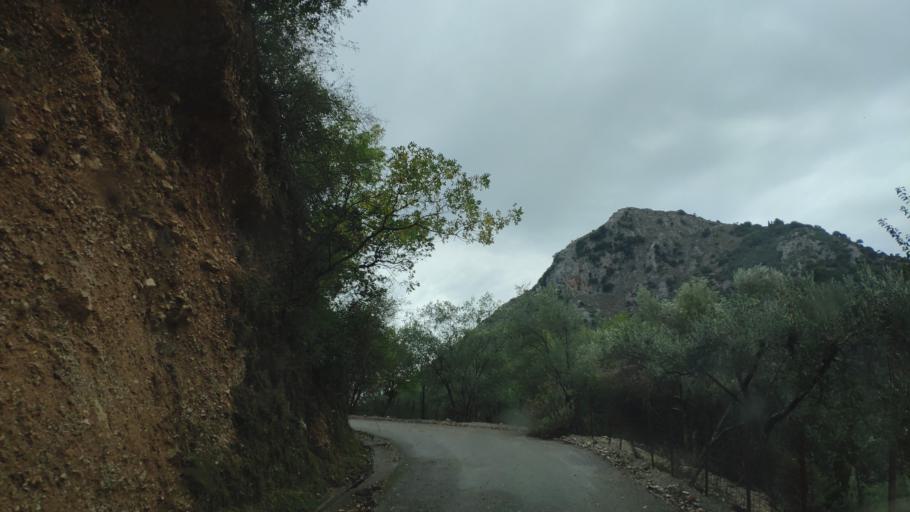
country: GR
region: Epirus
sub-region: Nomos Prevezis
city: Kanalaki
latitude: 39.3459
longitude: 20.6509
